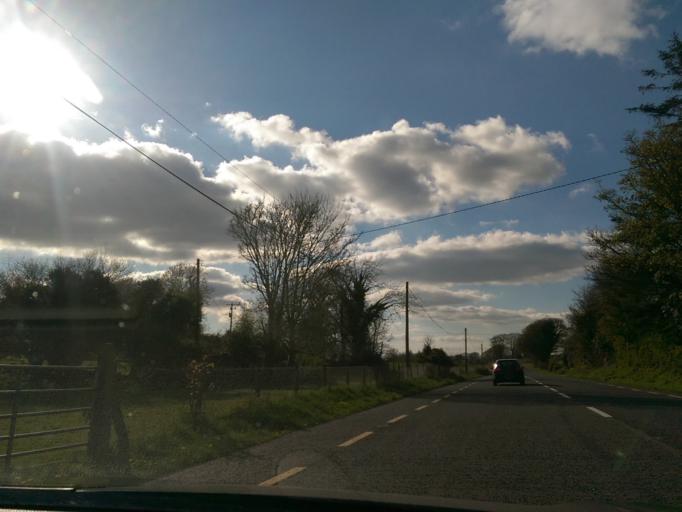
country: IE
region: Connaught
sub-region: County Galway
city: Portumna
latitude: 53.1801
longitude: -8.3468
